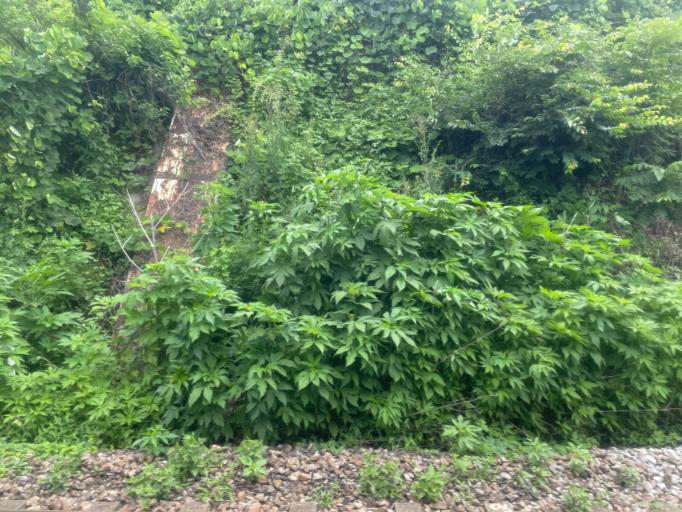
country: JP
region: Gunma
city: Numata
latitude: 36.6826
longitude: 138.9968
